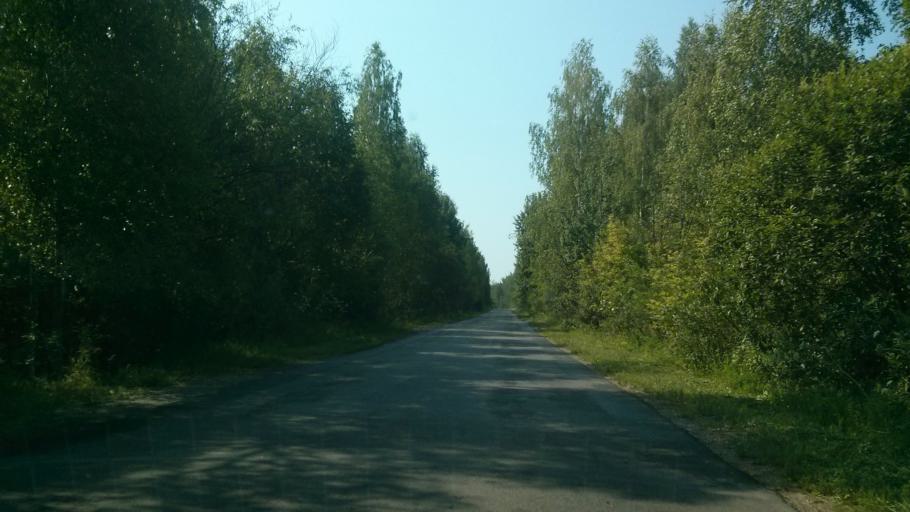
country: RU
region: Vladimir
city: Murom
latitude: 55.5233
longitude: 42.0220
